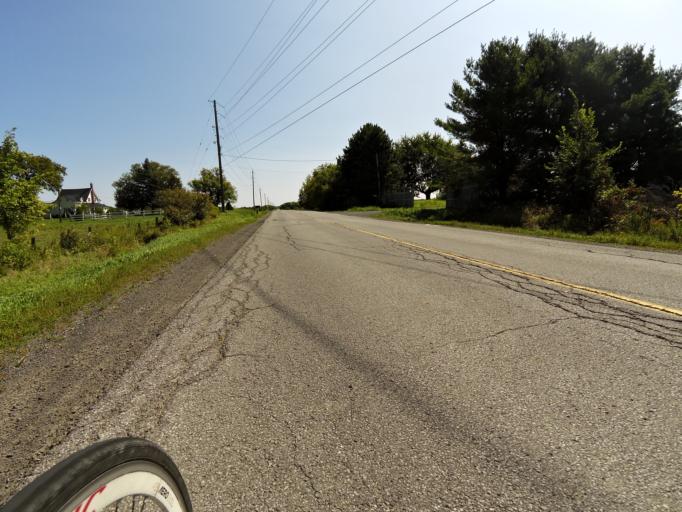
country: CA
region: Ontario
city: Arnprior
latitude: 45.4706
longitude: -76.1099
